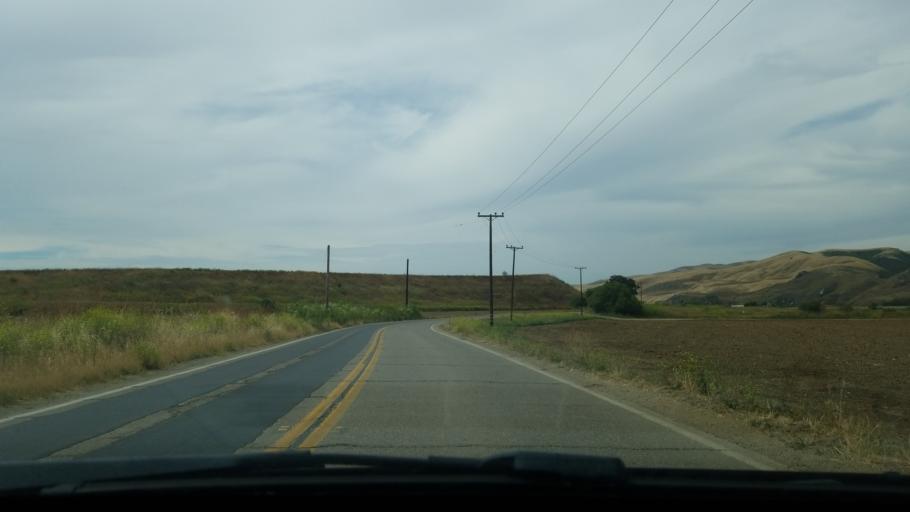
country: US
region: California
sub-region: Santa Barbara County
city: Orcutt
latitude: 34.9007
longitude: -120.3160
